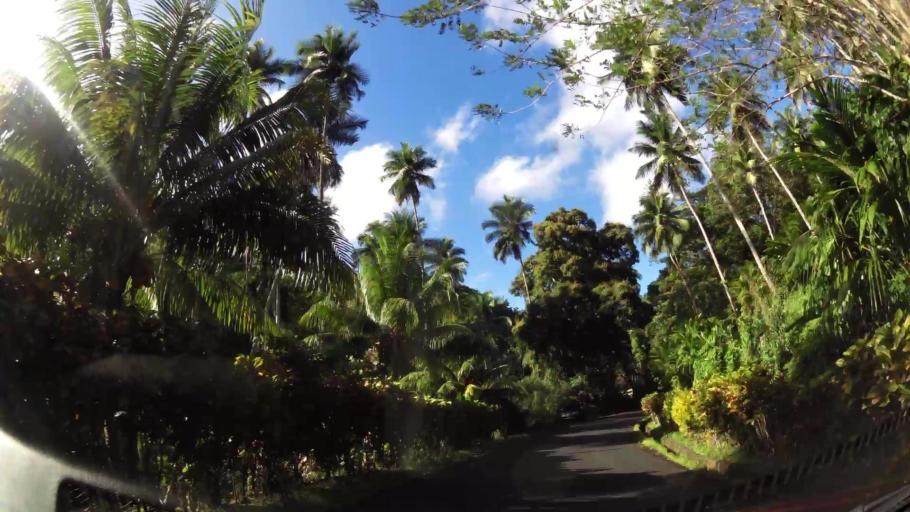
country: DM
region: Saint Andrew
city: Calibishie
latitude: 15.5893
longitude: -61.3968
